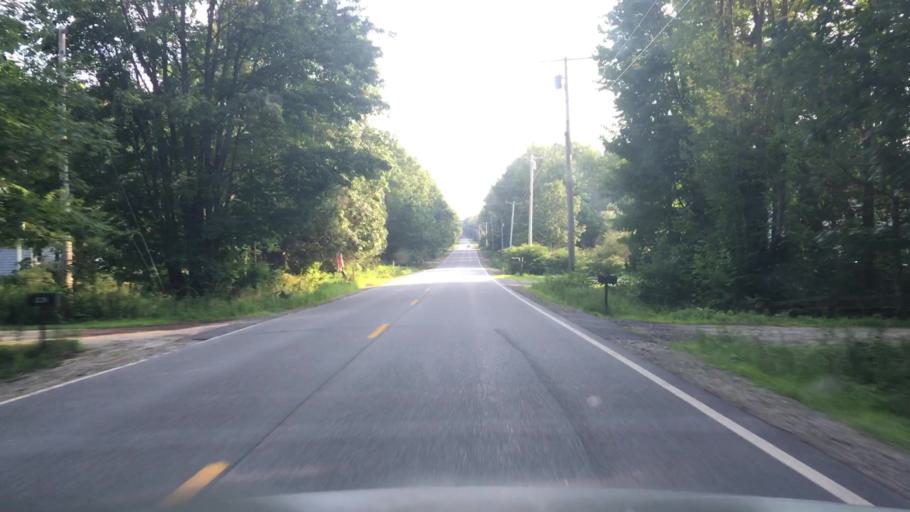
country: US
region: Maine
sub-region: Androscoggin County
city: Lisbon Falls
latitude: 43.9356
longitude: -70.0804
